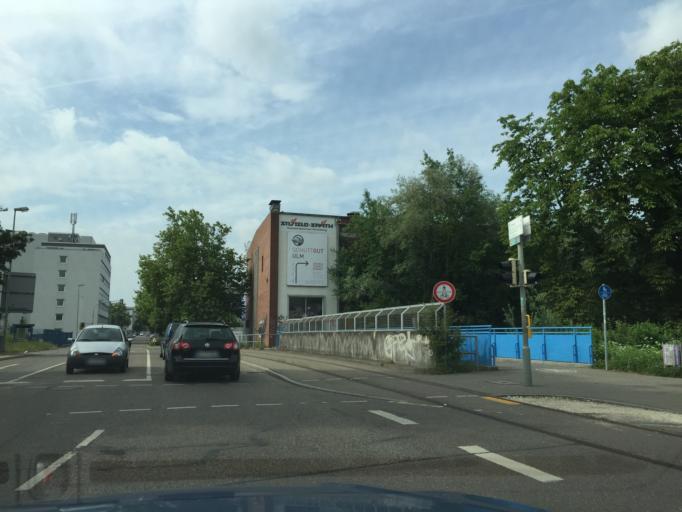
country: DE
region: Baden-Wuerttemberg
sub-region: Tuebingen Region
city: Ulm
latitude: 48.3988
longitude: 9.9647
